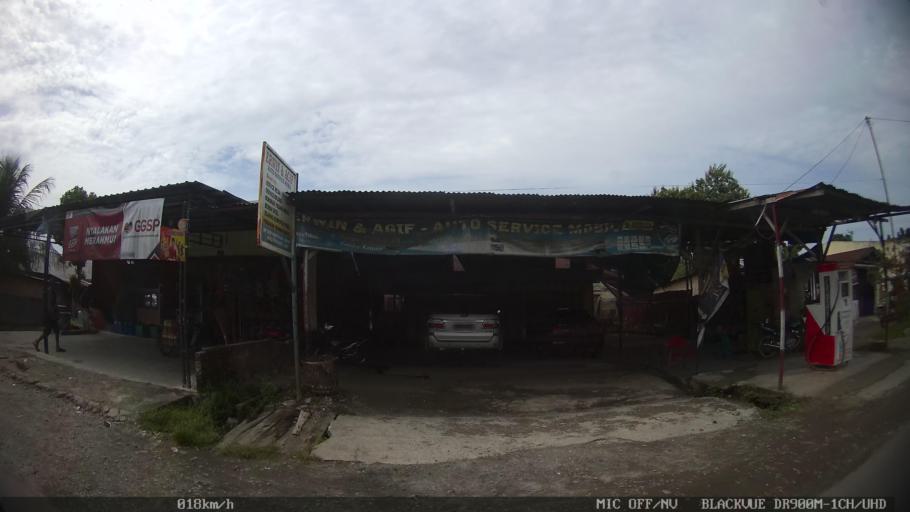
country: ID
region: North Sumatra
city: Percut
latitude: 3.6199
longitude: 98.7820
